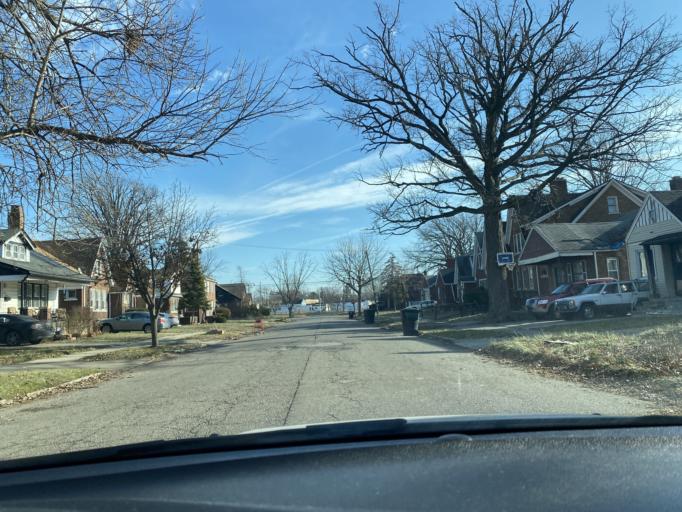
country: US
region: Michigan
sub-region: Wayne County
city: Harper Woods
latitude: 42.4125
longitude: -82.9472
